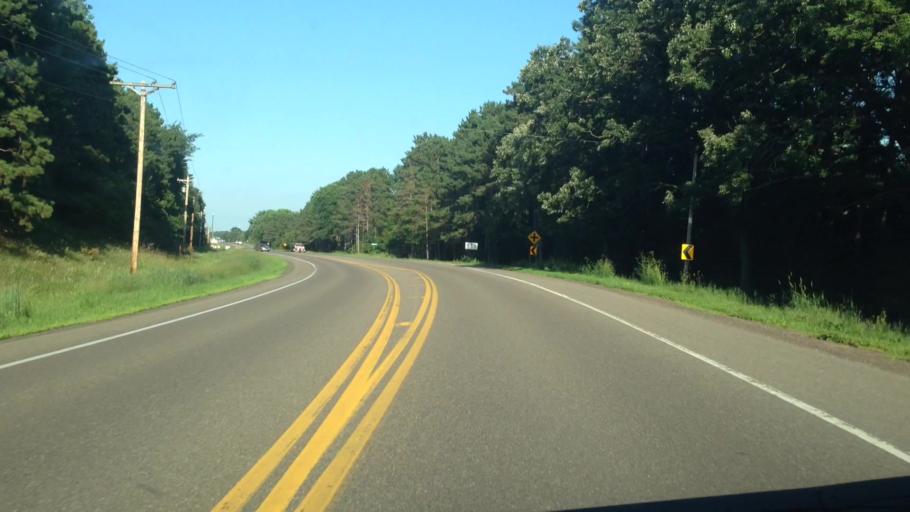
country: US
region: Minnesota
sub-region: Sherburne County
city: Zimmerman
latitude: 45.4439
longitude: -93.6222
